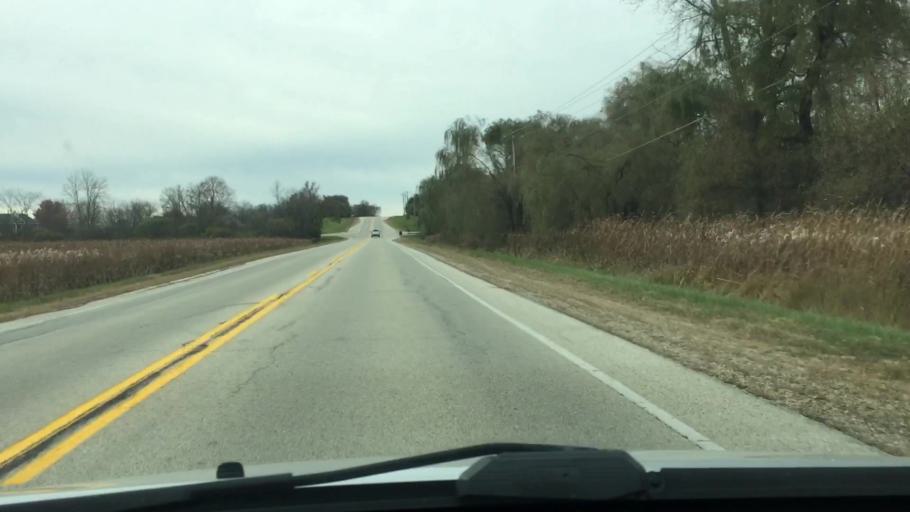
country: US
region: Wisconsin
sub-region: Waukesha County
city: Mukwonago
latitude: 42.8907
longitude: -88.2795
